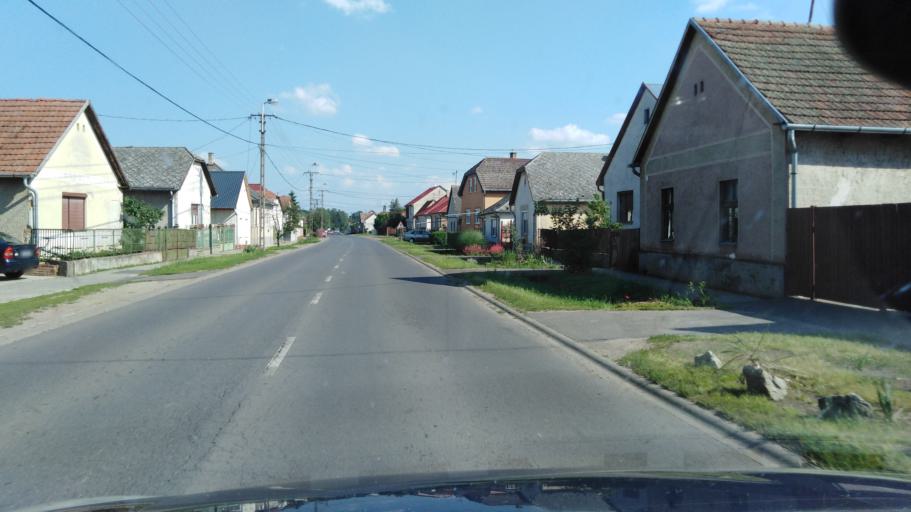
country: HU
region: Szabolcs-Szatmar-Bereg
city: Nyirbator
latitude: 47.8304
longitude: 22.1391
